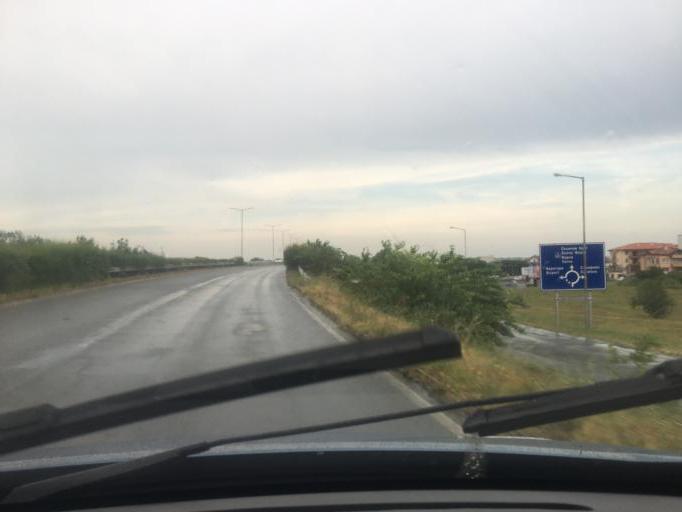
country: BG
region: Burgas
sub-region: Obshtina Burgas
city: Burgas
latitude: 42.5629
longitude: 27.5173
